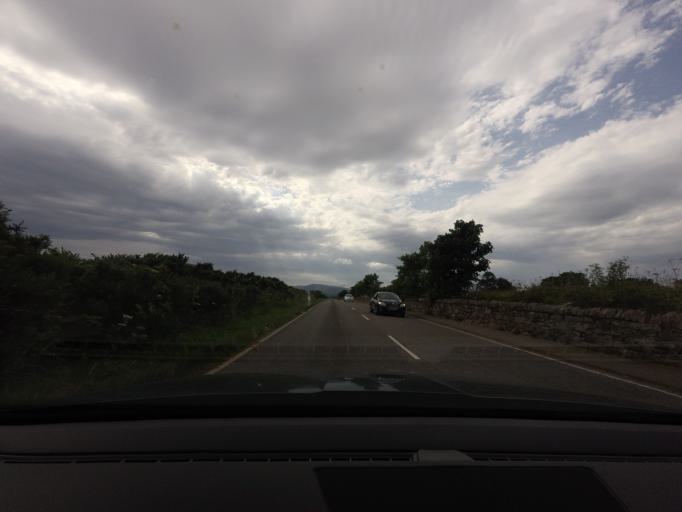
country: GB
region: Scotland
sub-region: Highland
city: Invergordon
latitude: 57.6914
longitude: -4.1901
